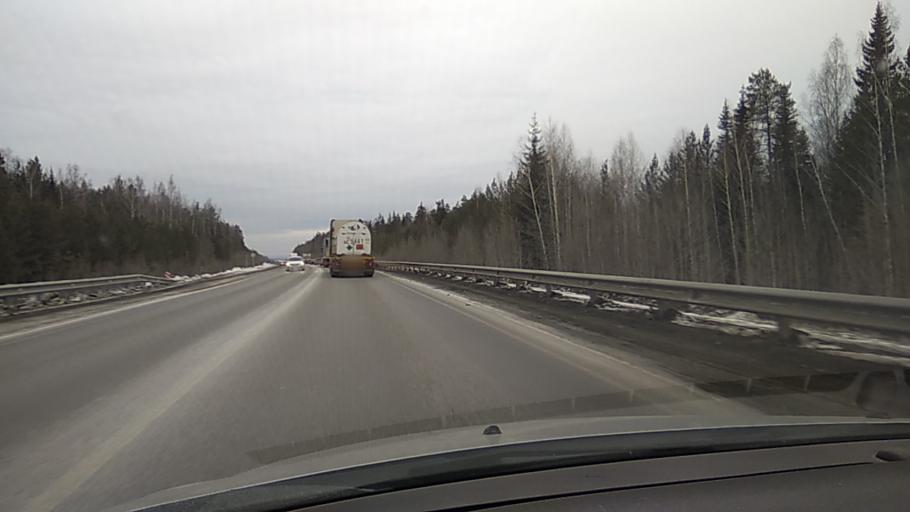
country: RU
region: Sverdlovsk
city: Talitsa
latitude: 56.8374
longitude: 60.0015
